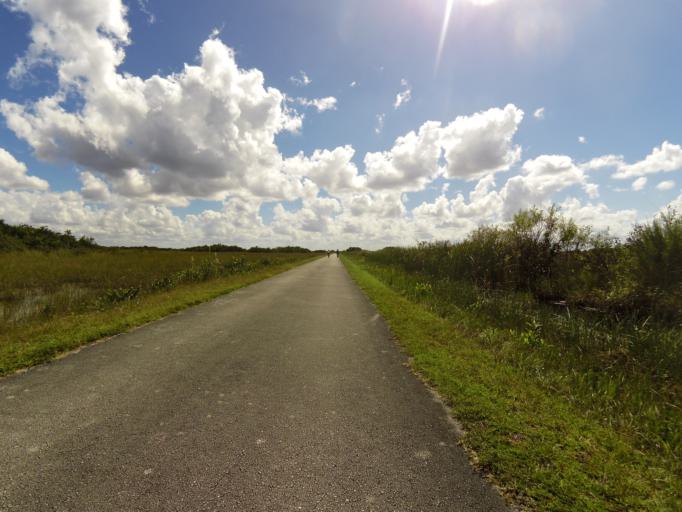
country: US
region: Florida
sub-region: Miami-Dade County
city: The Hammocks
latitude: 25.7031
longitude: -80.7668
